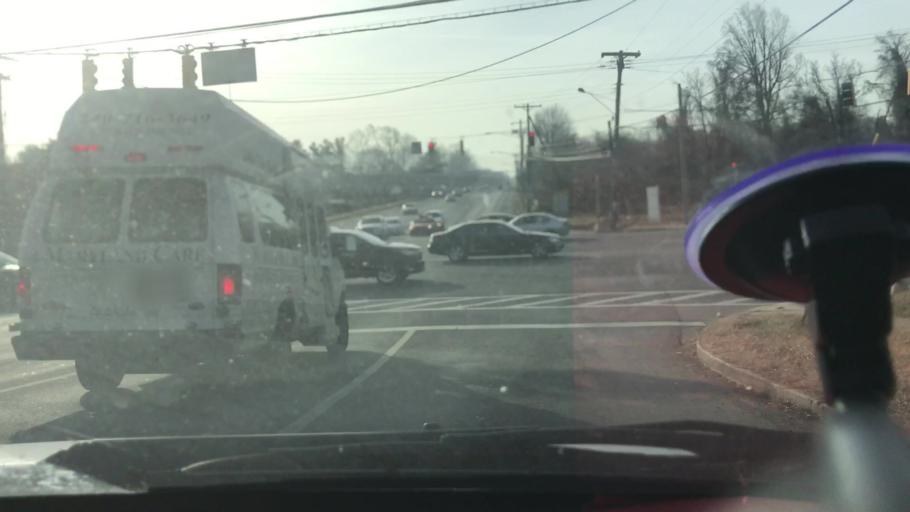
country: US
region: Maryland
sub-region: Prince George's County
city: Seat Pleasant
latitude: 38.8871
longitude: -76.8983
